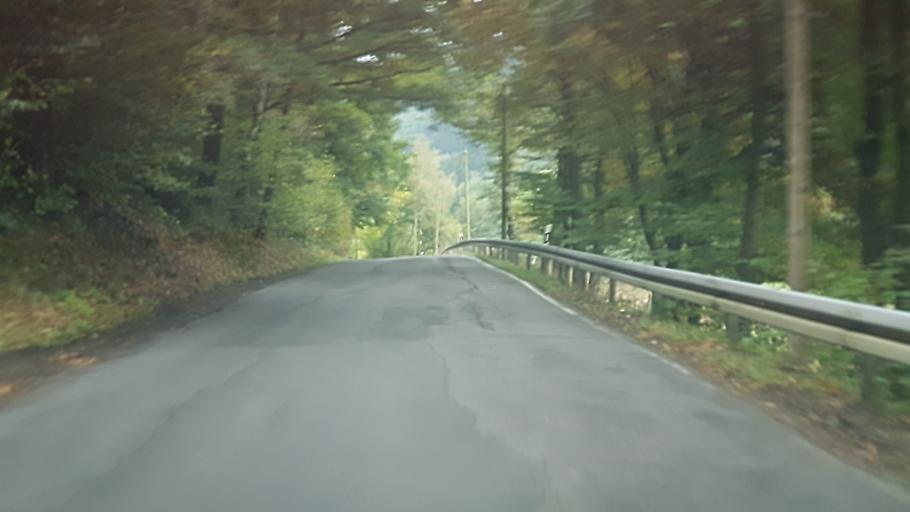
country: DE
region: North Rhine-Westphalia
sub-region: Regierungsbezirk Arnsberg
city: Herscheid
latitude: 51.1602
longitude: 7.7751
